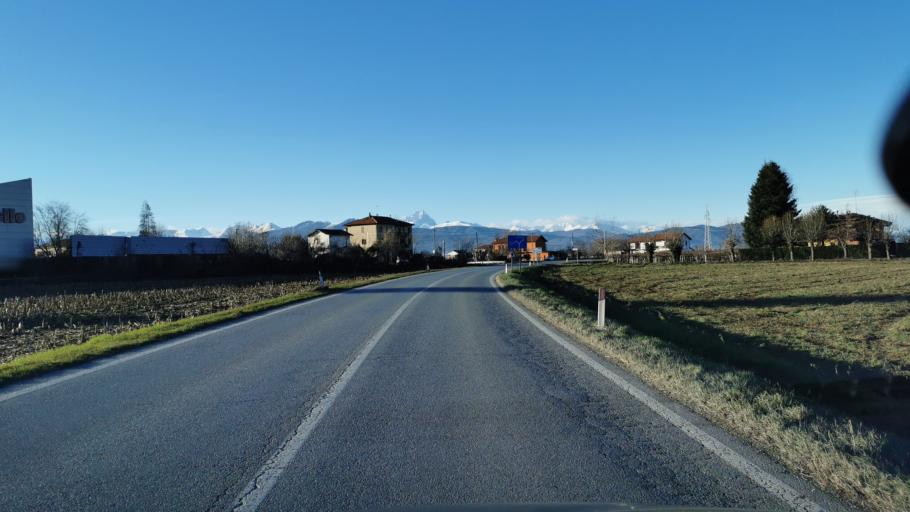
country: IT
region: Piedmont
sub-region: Provincia di Cuneo
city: Roata Rossi
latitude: 44.4268
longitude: 7.5467
